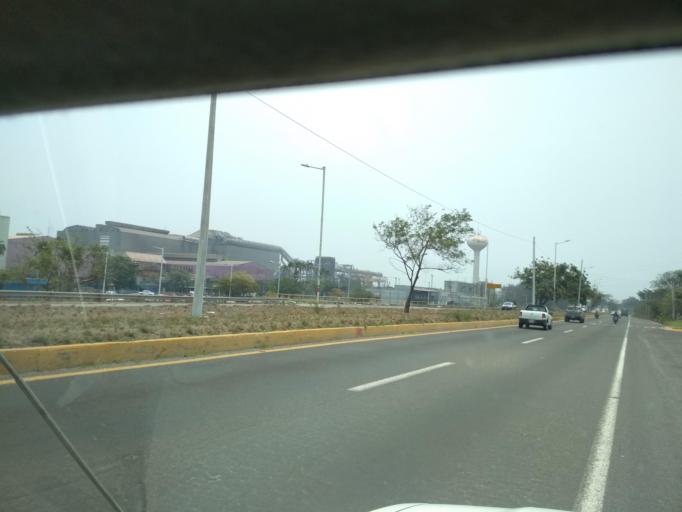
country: MX
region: Veracruz
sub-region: Veracruz
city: Oasis
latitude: 19.1775
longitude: -96.2452
